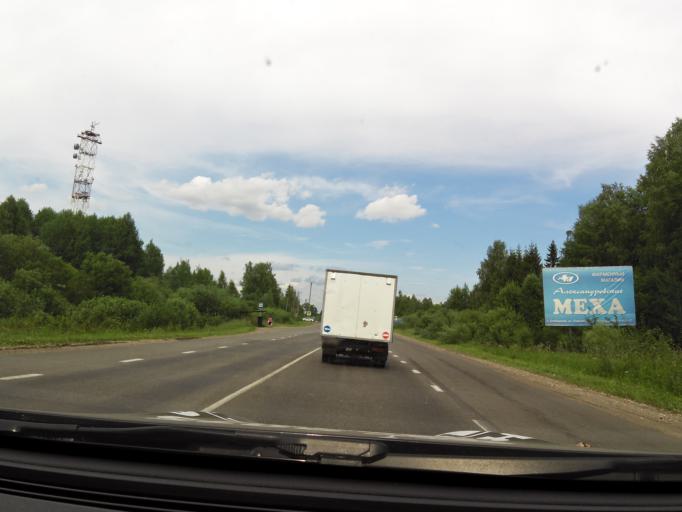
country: RU
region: Kirov
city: Stulovo
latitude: 58.6989
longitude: 50.0876
